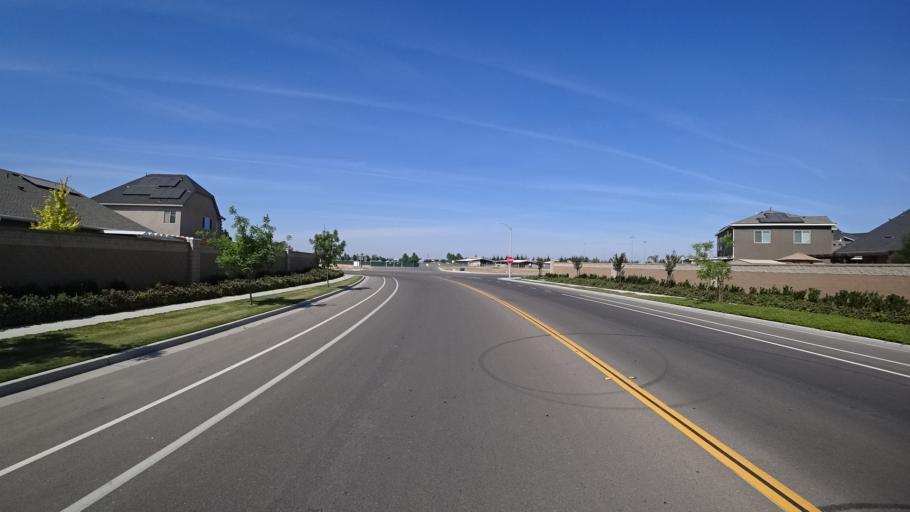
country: US
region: California
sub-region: Kings County
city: Armona
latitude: 36.3361
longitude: -119.6802
